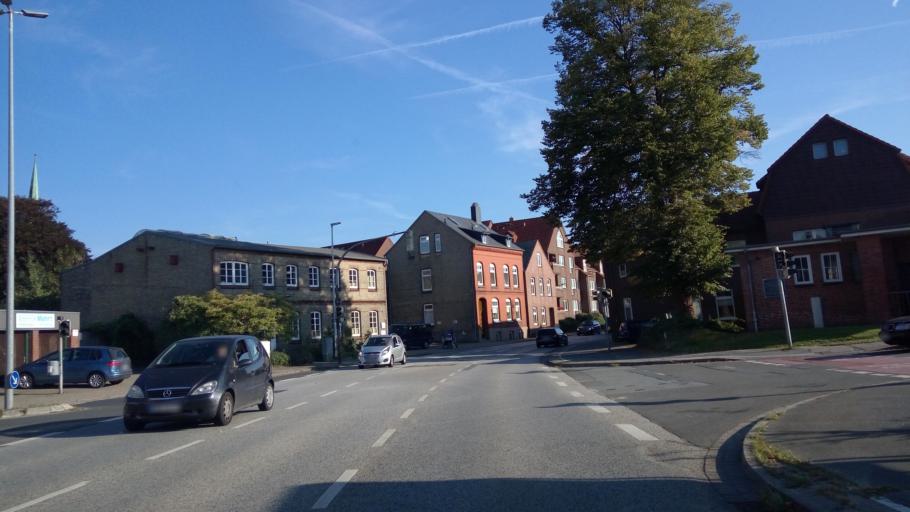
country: DE
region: Schleswig-Holstein
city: Eckernforde
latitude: 54.4726
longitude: 9.8334
